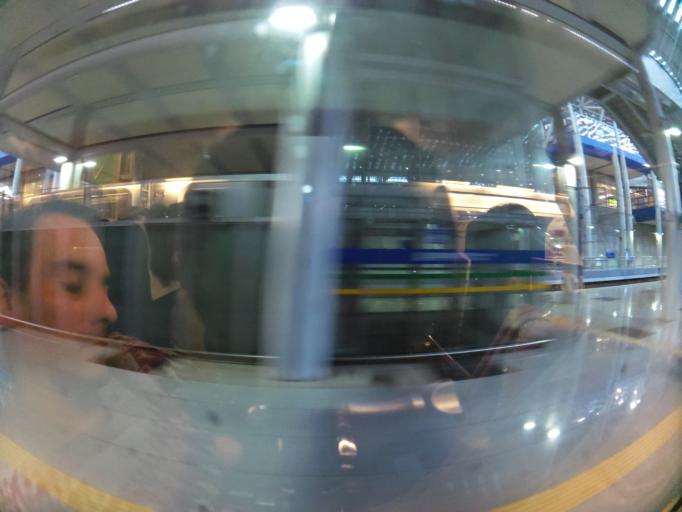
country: KR
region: Gyeonggi-do
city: Anyang-si
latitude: 37.4160
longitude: 126.8840
